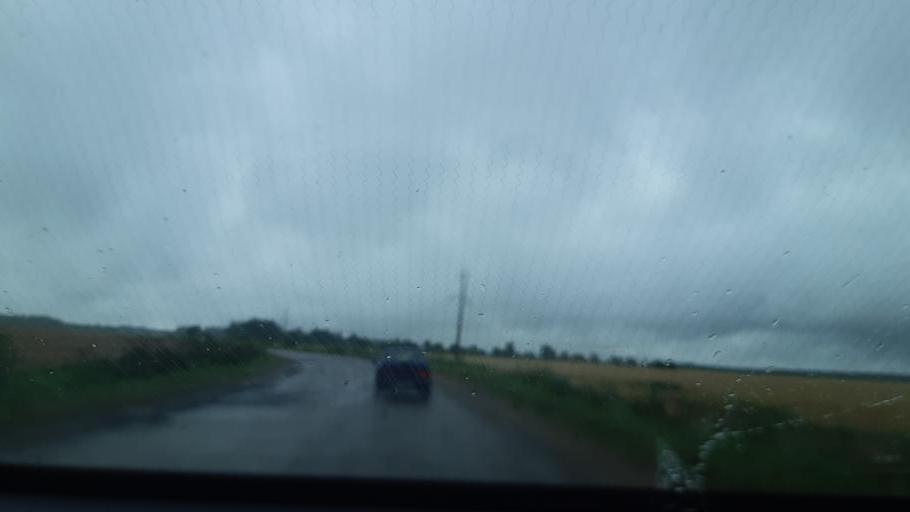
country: RU
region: Smolensk
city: Gagarin
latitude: 55.6364
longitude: 34.7550
